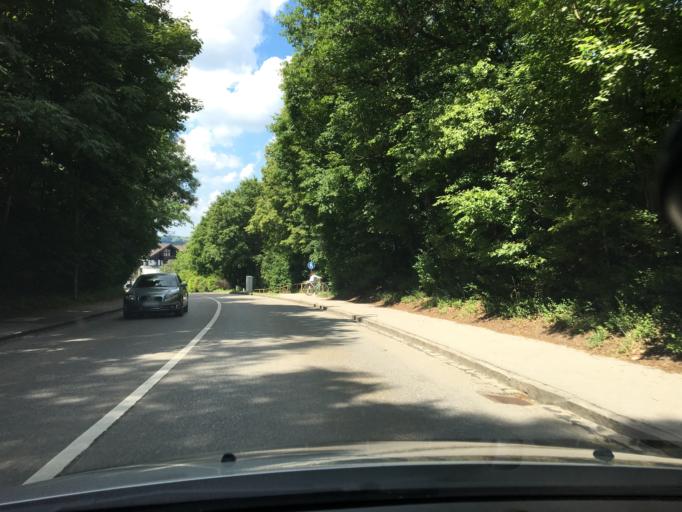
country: DE
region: Bavaria
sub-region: Upper Bavaria
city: Burgkirchen an der Alz
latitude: 48.1664
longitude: 12.7334
